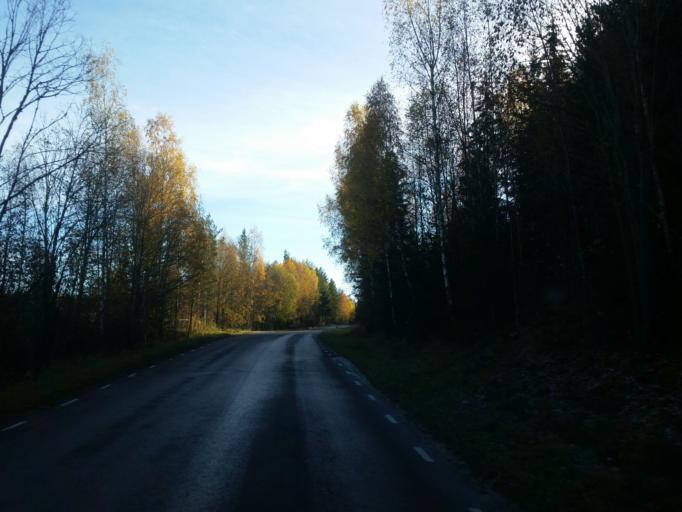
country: SE
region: Dalarna
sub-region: Borlange Kommun
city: Ornas
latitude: 60.5212
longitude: 15.5119
